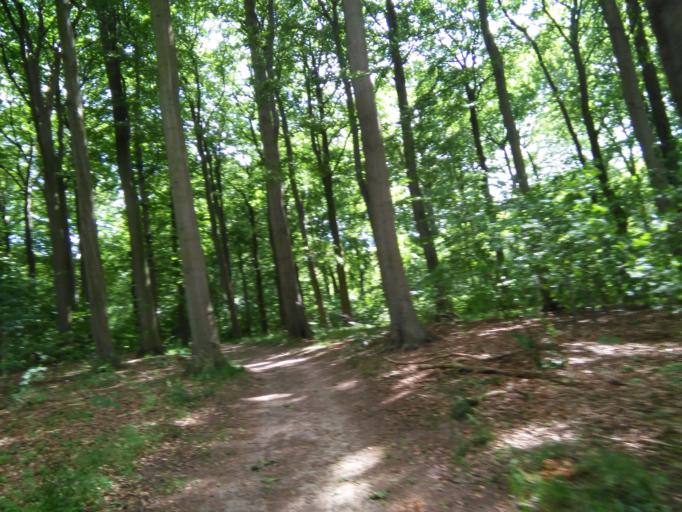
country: DK
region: Central Jutland
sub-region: Arhus Kommune
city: Arhus
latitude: 56.1319
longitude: 10.2008
